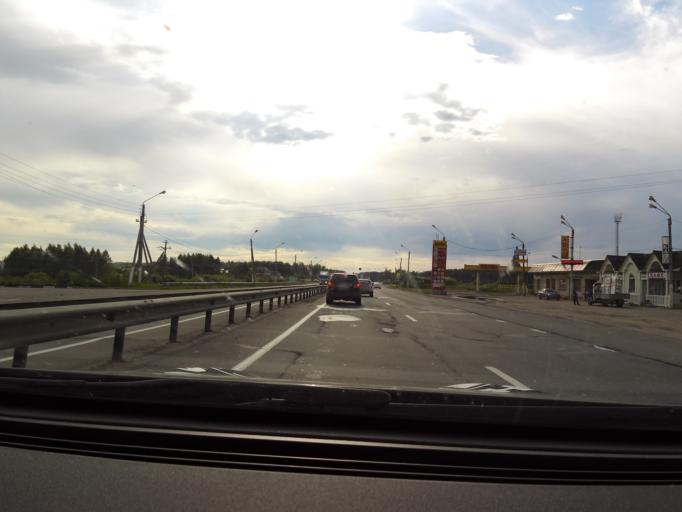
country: RU
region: Vladimir
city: Novovyazniki
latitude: 56.2191
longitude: 42.1893
